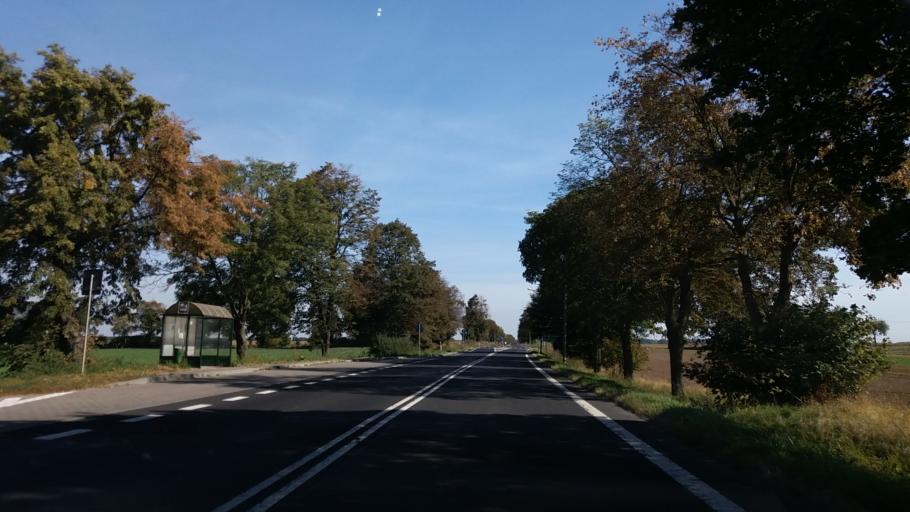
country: PL
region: Greater Poland Voivodeship
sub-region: Powiat miedzychodzki
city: Kwilcz
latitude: 52.5645
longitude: 16.0280
